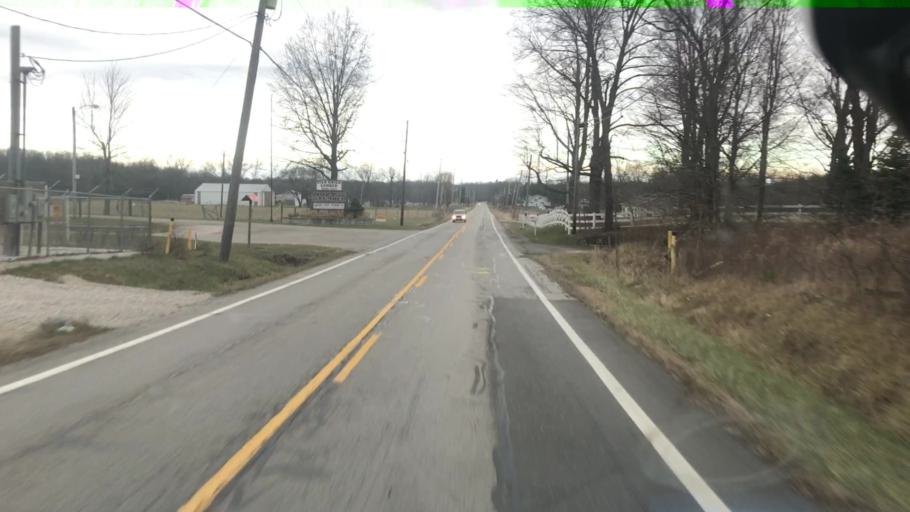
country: US
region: Ohio
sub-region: Trumbull County
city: Newton Falls
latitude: 41.2532
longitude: -80.9775
